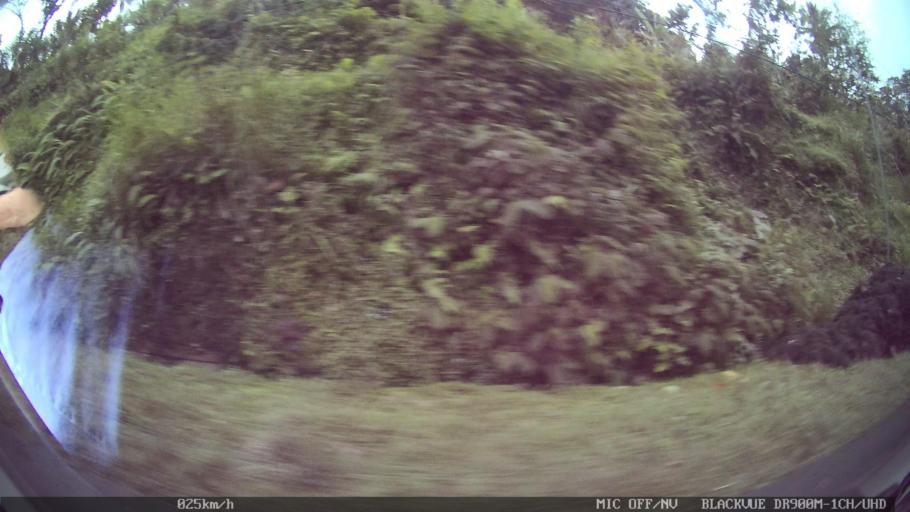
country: ID
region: Bali
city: Peneng
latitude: -8.3618
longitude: 115.2172
